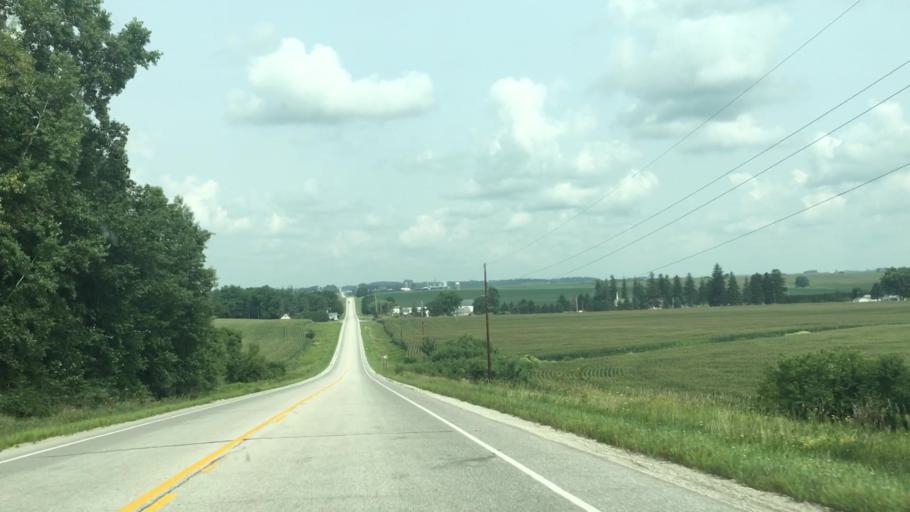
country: US
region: Minnesota
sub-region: Fillmore County
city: Harmony
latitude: 43.5885
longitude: -91.9298
